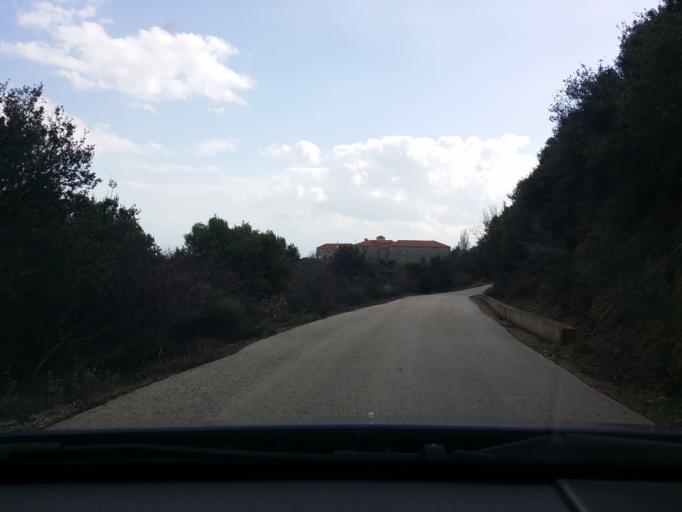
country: GR
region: West Greece
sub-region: Nomos Aitolias kai Akarnanias
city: Fitiai
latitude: 38.6523
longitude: 21.1974
